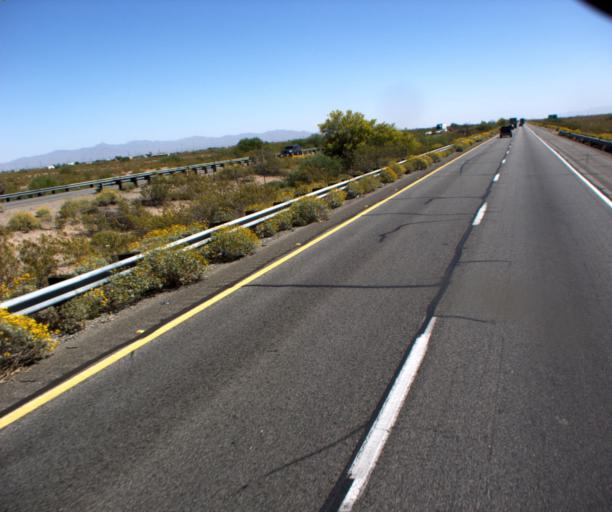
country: US
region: Arizona
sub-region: Maricopa County
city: Buckeye
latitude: 33.4787
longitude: -112.8542
